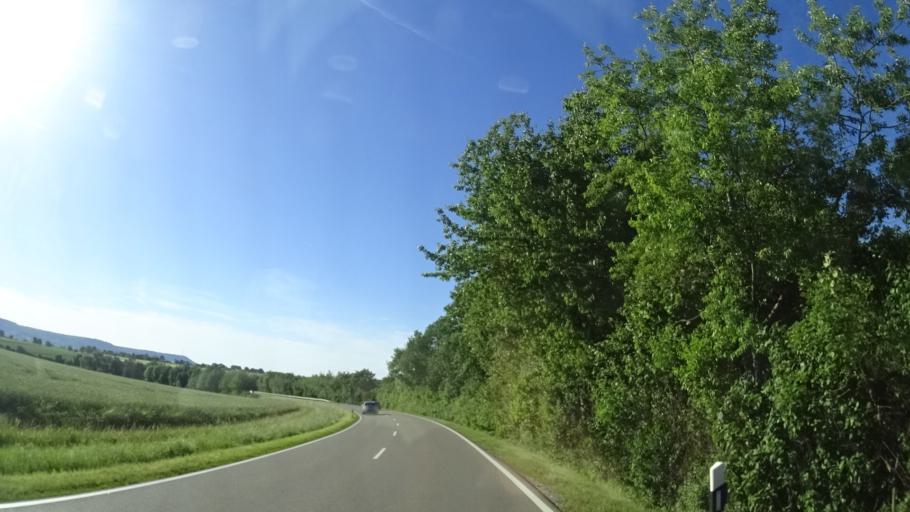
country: DE
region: Baden-Wuerttemberg
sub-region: Regierungsbezirk Stuttgart
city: Schwaebisch Hall
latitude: 49.1337
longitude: 9.7616
